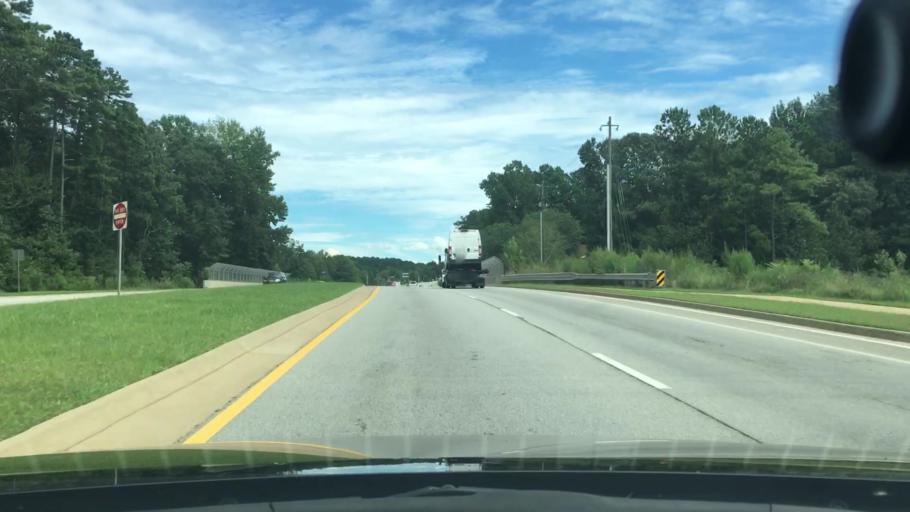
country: US
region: Georgia
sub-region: Coweta County
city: Newnan
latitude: 33.4006
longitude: -84.7770
